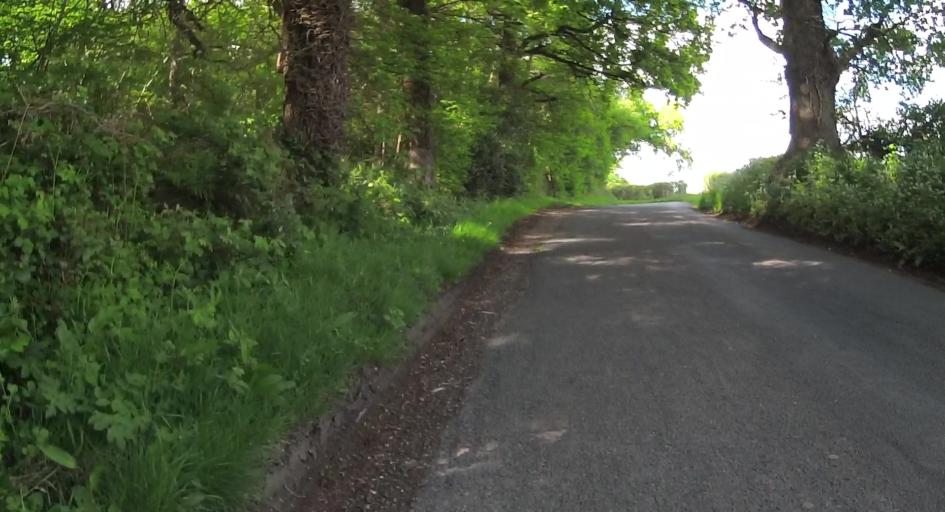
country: GB
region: England
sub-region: West Berkshire
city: Stratfield Mortimer
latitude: 51.3562
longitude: -1.0439
